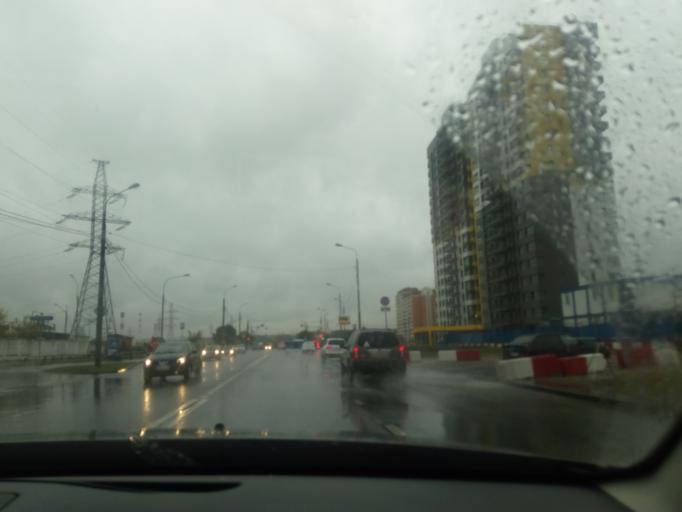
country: RU
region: Moscow
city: Zhulebino
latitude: 55.7119
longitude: 37.8777
